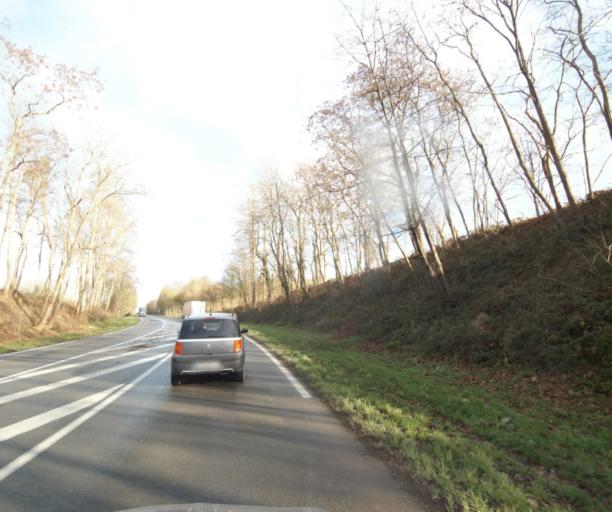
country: FR
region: Nord-Pas-de-Calais
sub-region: Departement du Nord
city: Famars
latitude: 50.3228
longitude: 3.5044
